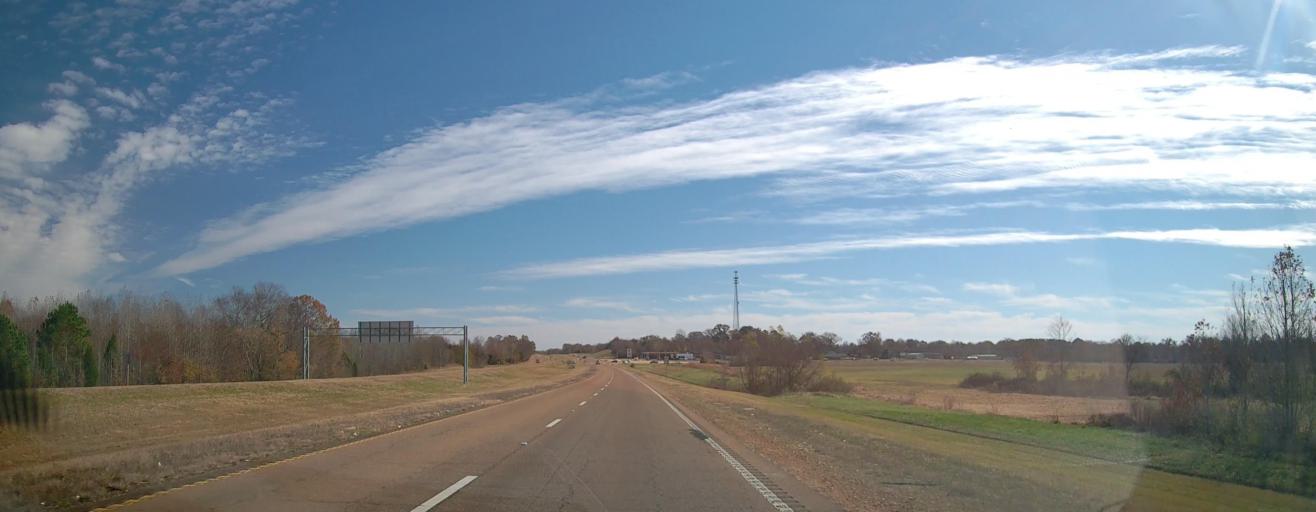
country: US
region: Tennessee
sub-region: Fayette County
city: Piperton
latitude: 34.9620
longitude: -89.5343
